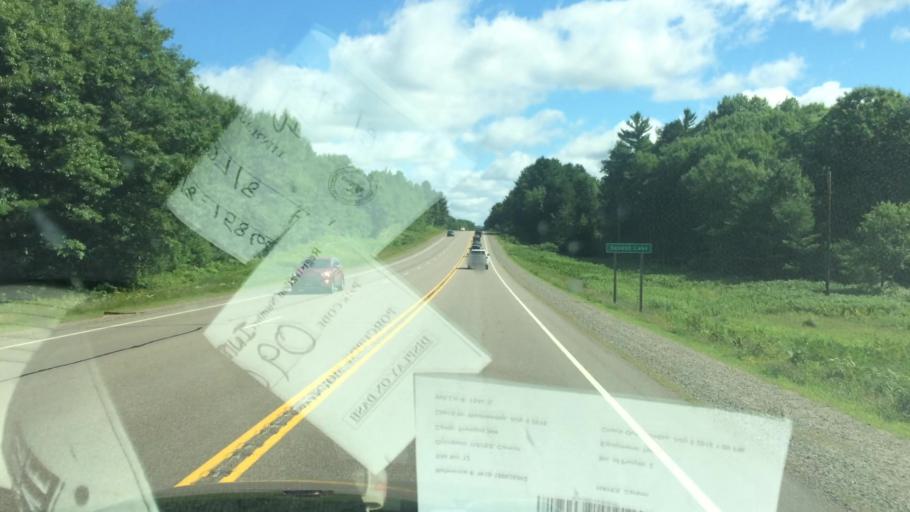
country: US
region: Wisconsin
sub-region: Oneida County
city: Rhinelander
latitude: 45.5958
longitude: -89.5650
